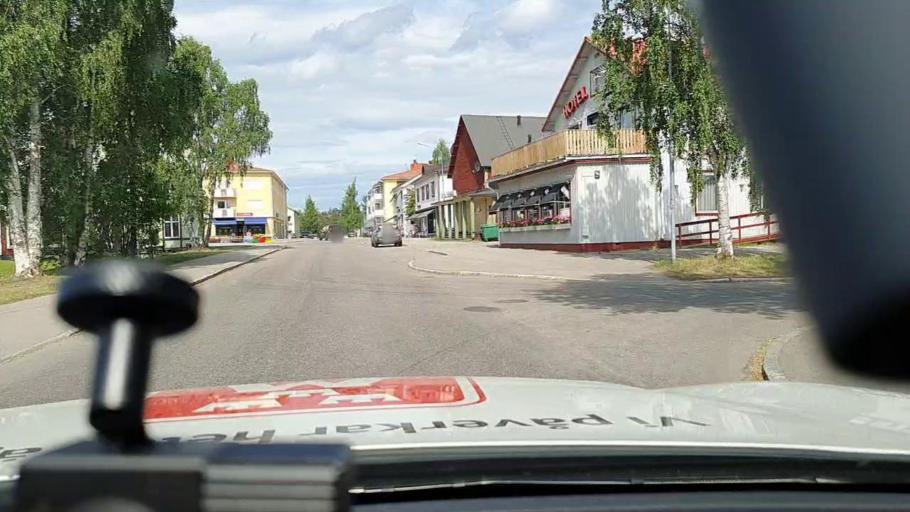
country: SE
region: Norrbotten
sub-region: Jokkmokks Kommun
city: Jokkmokk
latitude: 66.6065
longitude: 19.8333
